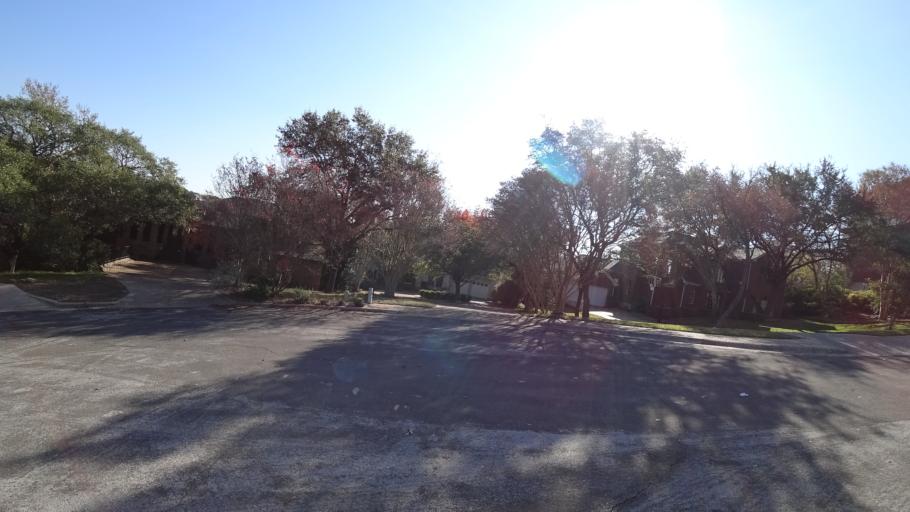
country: US
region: Texas
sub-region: Williamson County
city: Jollyville
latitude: 30.3930
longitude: -97.7666
